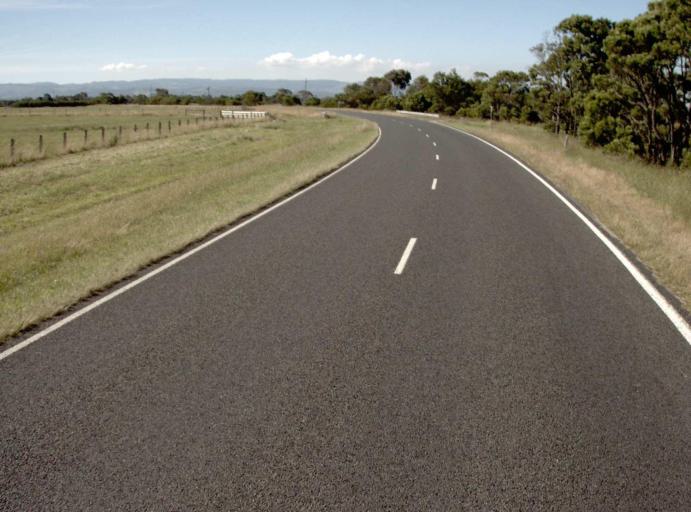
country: AU
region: Victoria
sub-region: Latrobe
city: Traralgon
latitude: -38.6289
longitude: 146.6766
